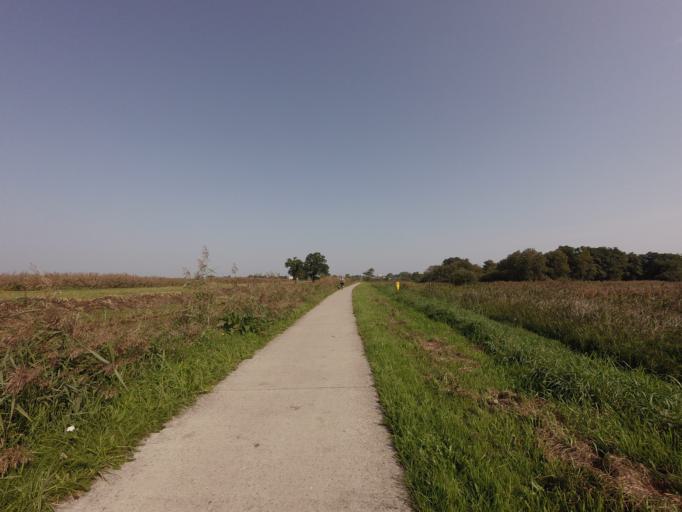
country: NL
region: Groningen
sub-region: Gemeente Groningen
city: Groningen
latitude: 53.1661
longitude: 6.5414
